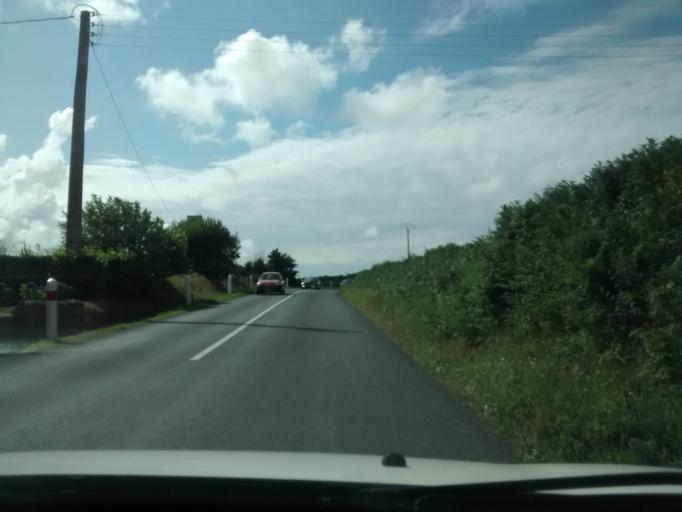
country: FR
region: Brittany
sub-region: Departement des Cotes-d'Armor
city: Penvenan
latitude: 48.7935
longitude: -3.2797
